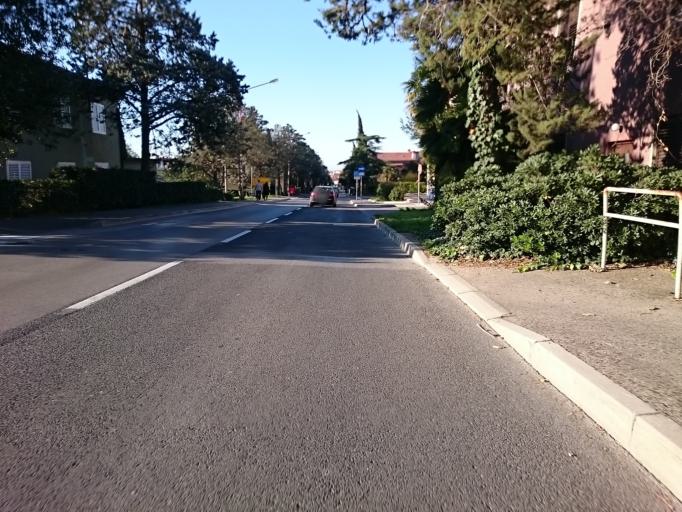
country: SI
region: Izola-Isola
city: Izola
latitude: 45.5320
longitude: 13.6659
